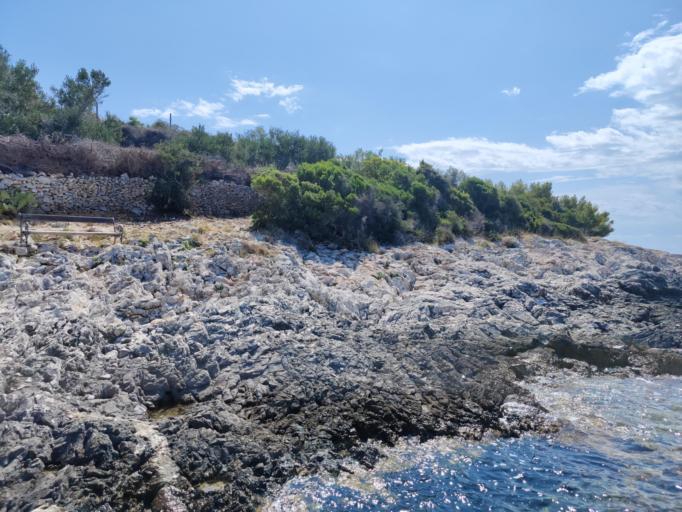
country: HR
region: Splitsko-Dalmatinska
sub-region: Grad Hvar
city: Hvar
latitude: 43.1631
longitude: 16.4558
